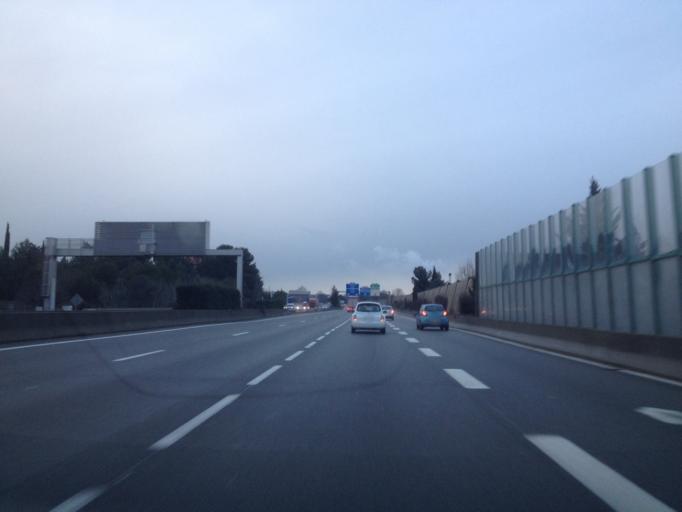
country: FR
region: Provence-Alpes-Cote d'Azur
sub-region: Departement des Bouches-du-Rhone
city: Aix-en-Provence
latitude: 43.5151
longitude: 5.4349
